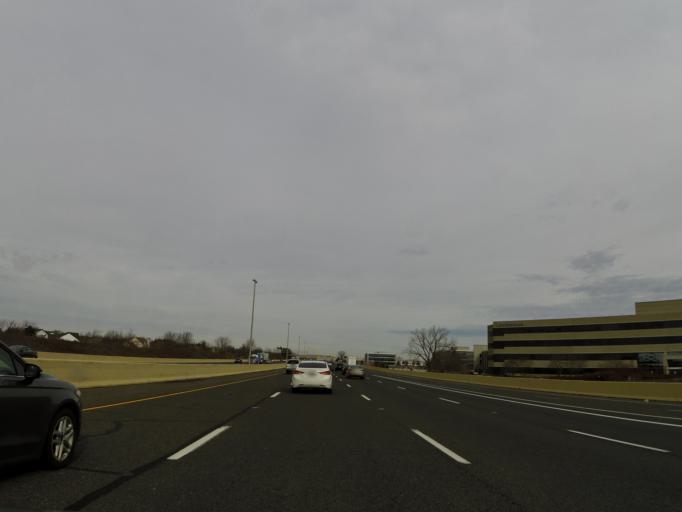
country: US
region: Indiana
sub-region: Boone County
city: Zionsville
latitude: 39.8870
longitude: -86.2693
